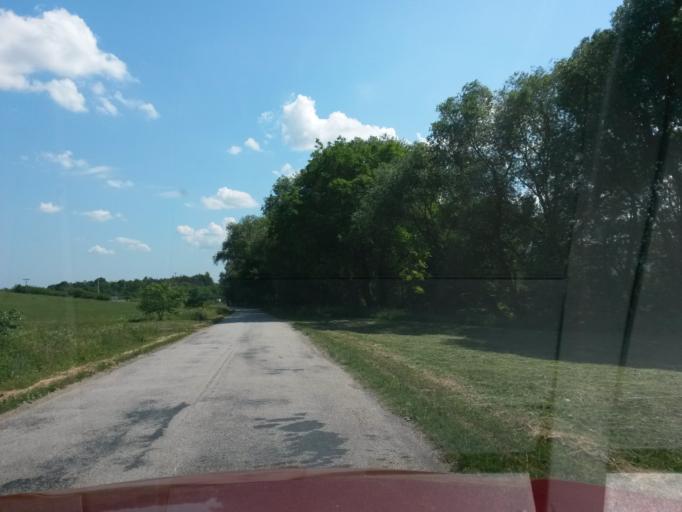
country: SK
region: Kosicky
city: Medzev
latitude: 48.6087
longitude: 20.8363
